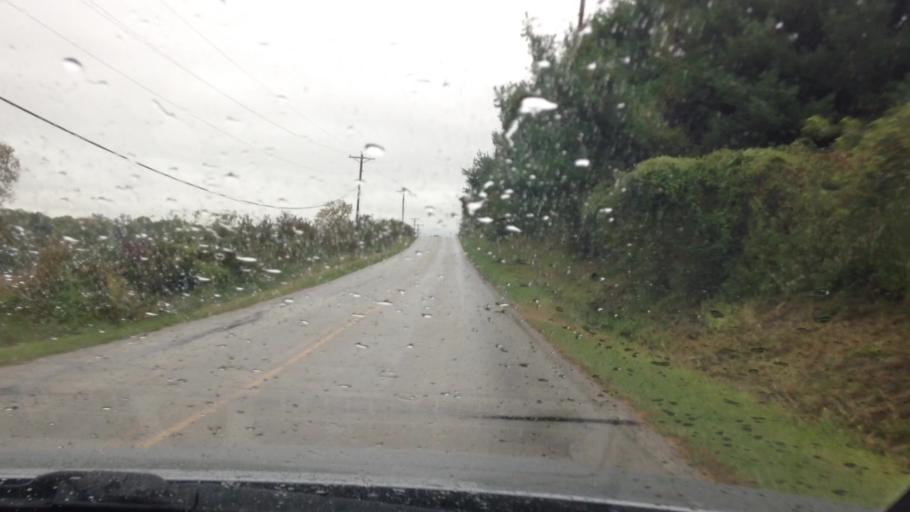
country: US
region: Missouri
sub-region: Platte County
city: Platte City
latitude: 39.3317
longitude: -94.8305
